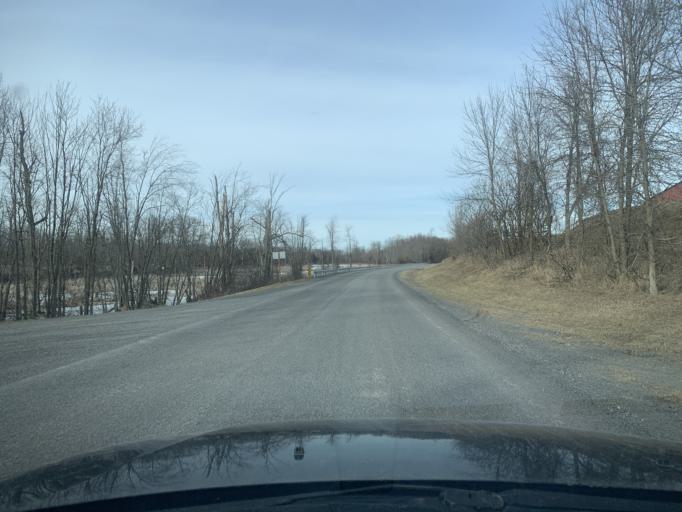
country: CA
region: Ontario
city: Greater Napanee
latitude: 44.4655
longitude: -77.0550
